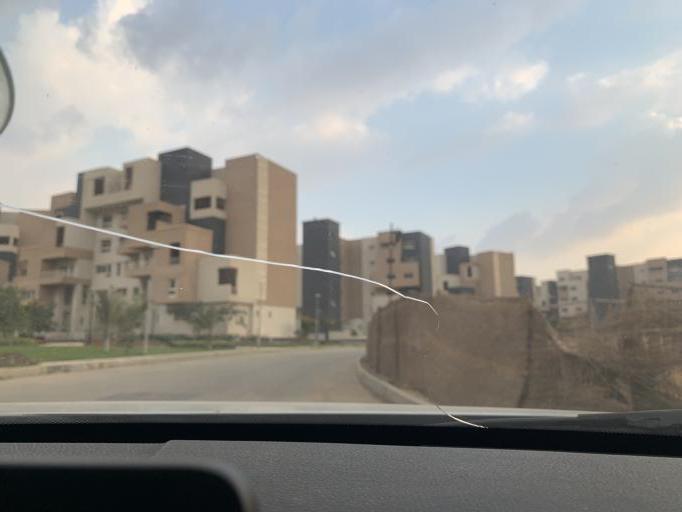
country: EG
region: Muhafazat al Qalyubiyah
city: Al Khankah
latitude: 30.1007
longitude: 31.6520
